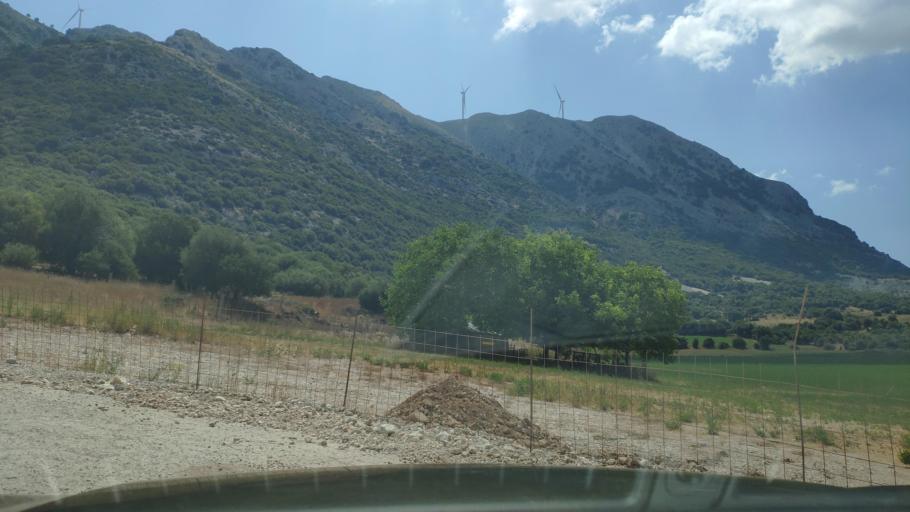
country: GR
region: West Greece
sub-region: Nomos Aitolias kai Akarnanias
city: Kandila
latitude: 38.7763
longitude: 20.9727
